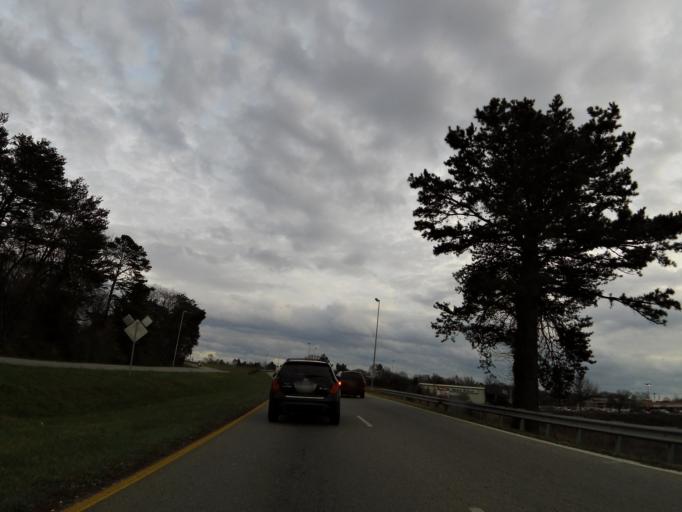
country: US
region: Tennessee
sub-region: Blount County
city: Maryville
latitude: 35.7424
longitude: -83.9917
